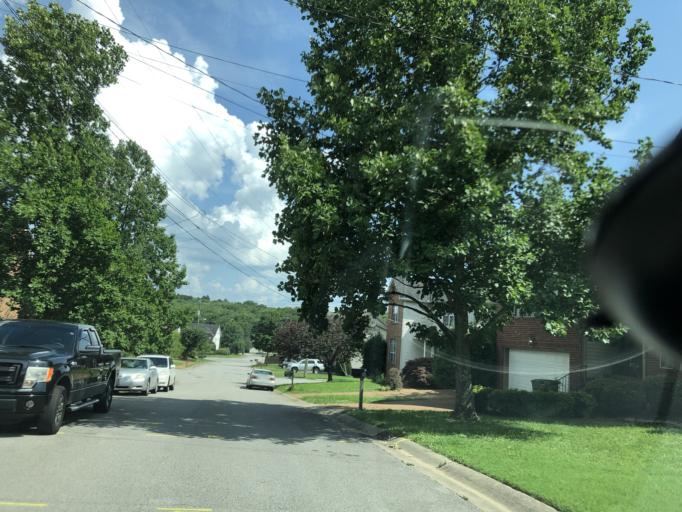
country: US
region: Tennessee
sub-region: Rutherford County
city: La Vergne
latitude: 36.0108
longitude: -86.6278
